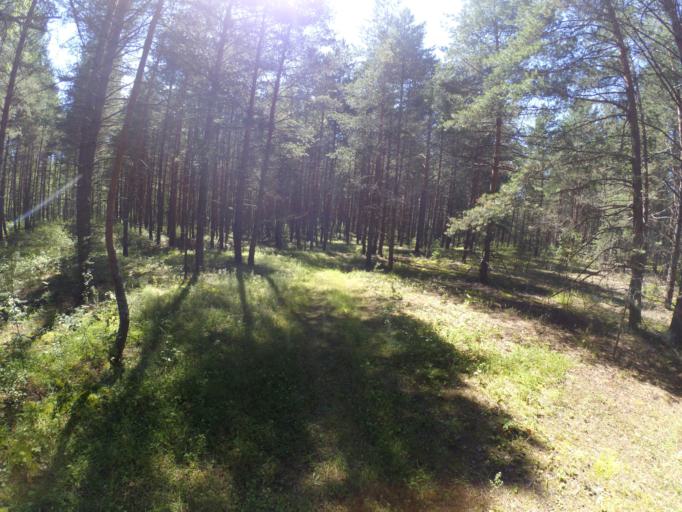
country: RU
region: Moskovskaya
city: Fosforitnyy
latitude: 55.3395
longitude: 38.9201
